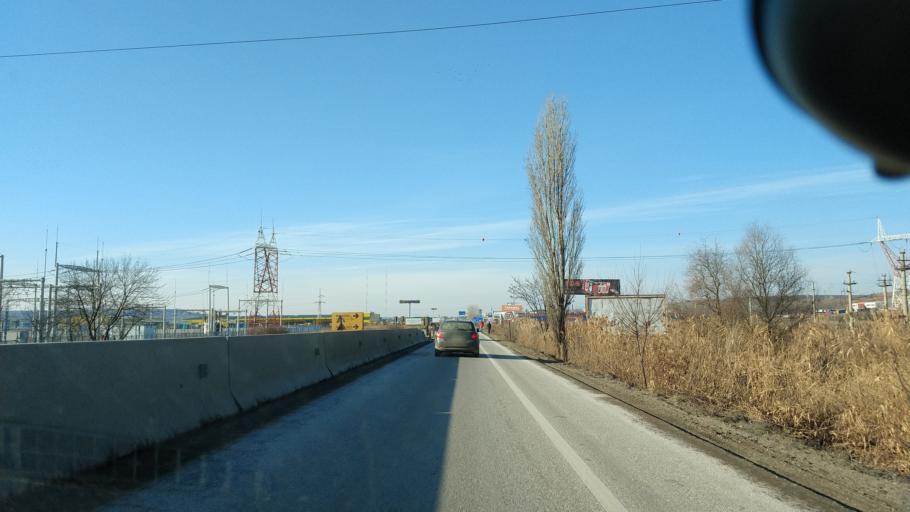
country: RO
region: Iasi
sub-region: Comuna Valea Lupului
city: Valea Lupului
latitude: 47.1788
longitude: 27.4827
